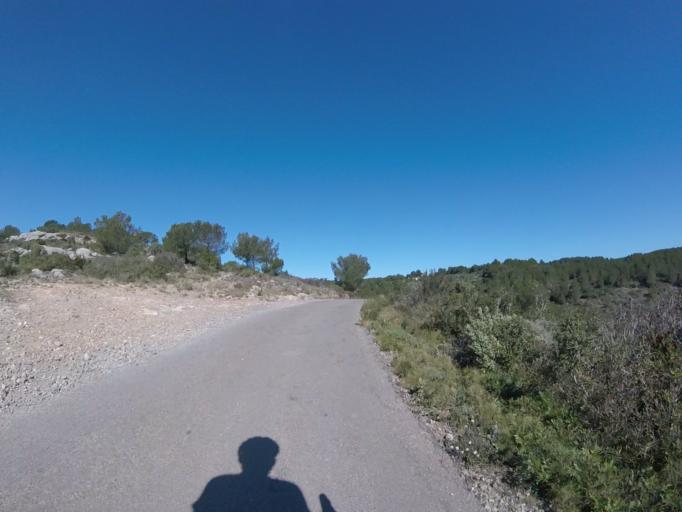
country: ES
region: Valencia
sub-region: Provincia de Castello
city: Benicassim
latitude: 40.0794
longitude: 0.0900
